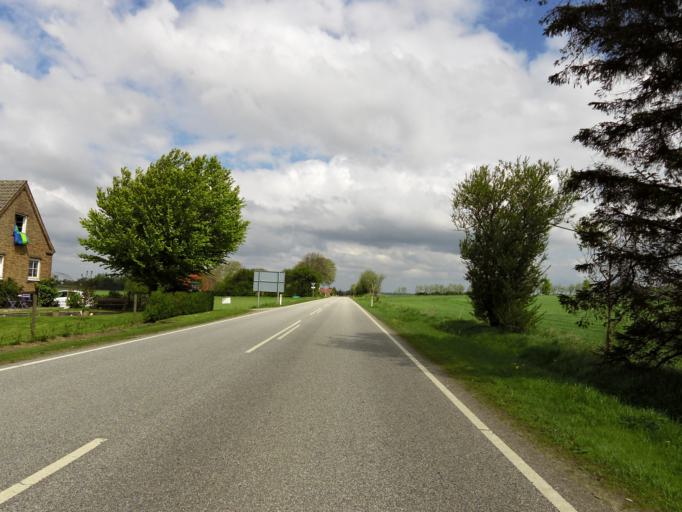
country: DK
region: South Denmark
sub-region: Haderslev Kommune
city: Gram
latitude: 55.2328
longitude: 8.9611
